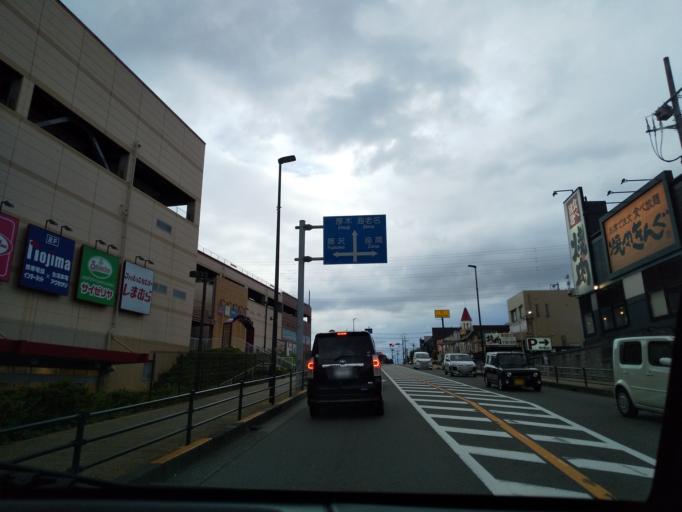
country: JP
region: Kanagawa
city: Minami-rinkan
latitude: 35.4375
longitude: 139.4293
